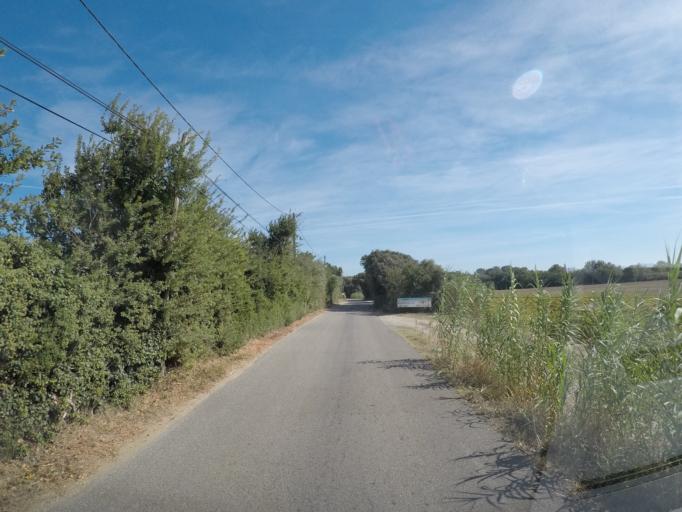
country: FR
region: Provence-Alpes-Cote d'Azur
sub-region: Departement du Vaucluse
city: Bollene
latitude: 44.2867
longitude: 4.7853
